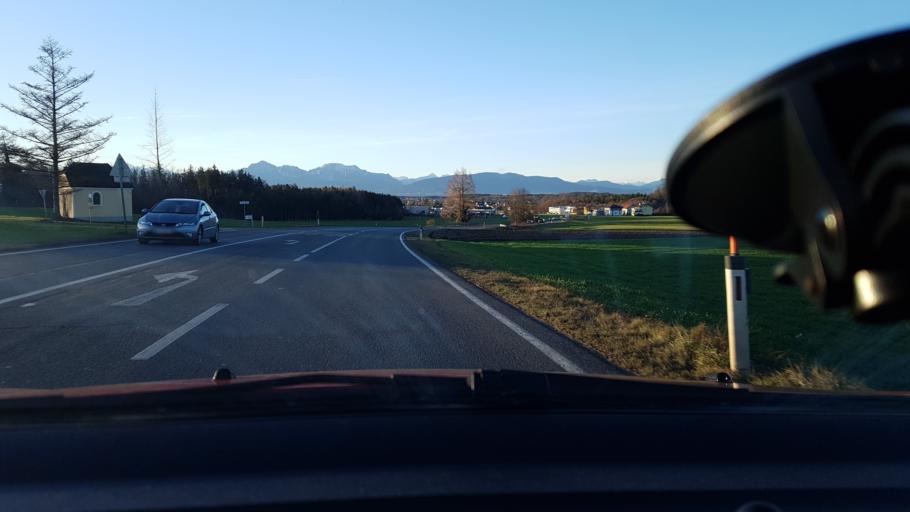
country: AT
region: Salzburg
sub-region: Politischer Bezirk Salzburg-Umgebung
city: Oberndorf bei Salzburg
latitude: 47.9627
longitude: 12.9471
